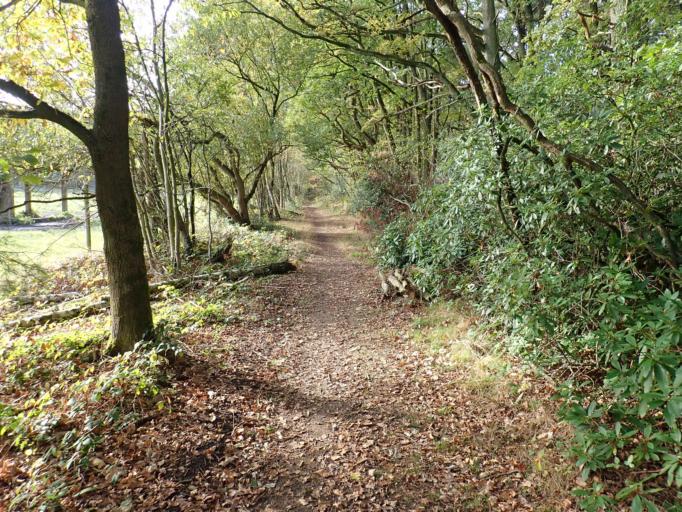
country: BE
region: Flanders
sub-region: Provincie Antwerpen
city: Zoersel
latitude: 51.2494
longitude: 4.6905
